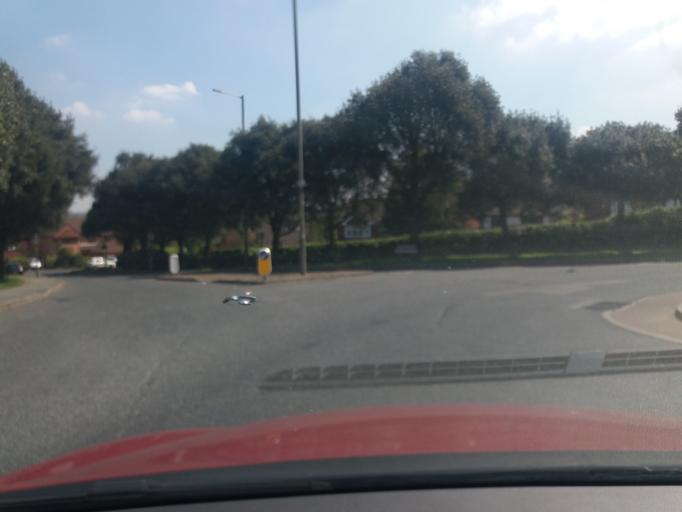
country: GB
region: England
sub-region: Lancashire
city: Chorley
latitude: 53.6779
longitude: -2.6354
